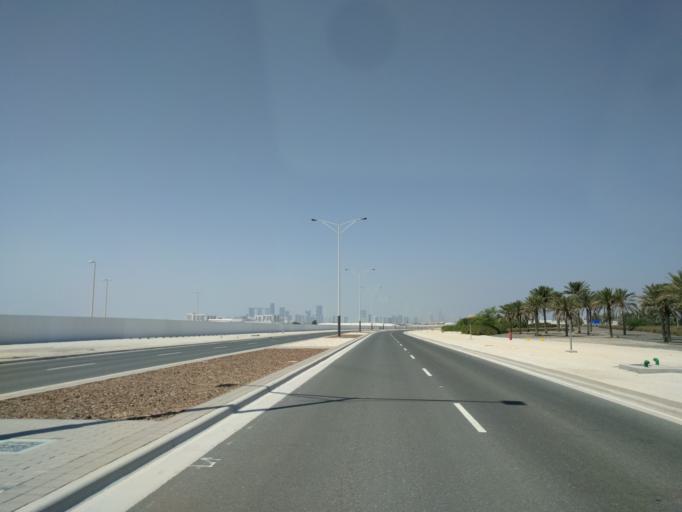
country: AE
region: Abu Dhabi
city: Abu Dhabi
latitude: 24.5449
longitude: 54.4497
